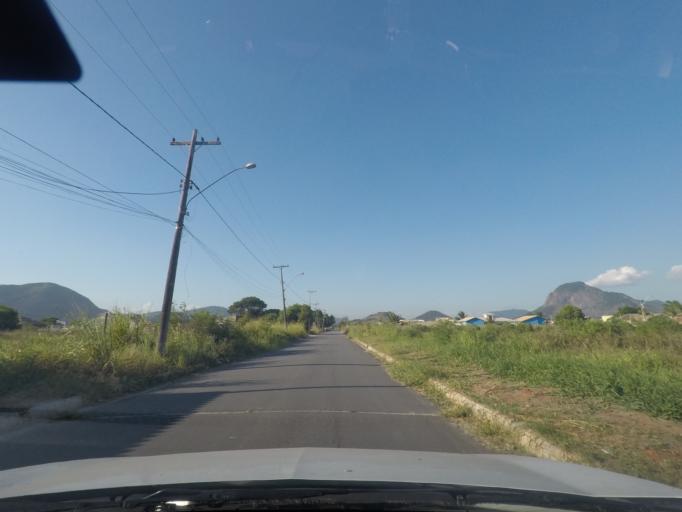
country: BR
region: Rio de Janeiro
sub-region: Marica
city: Marica
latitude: -22.9626
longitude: -42.9388
